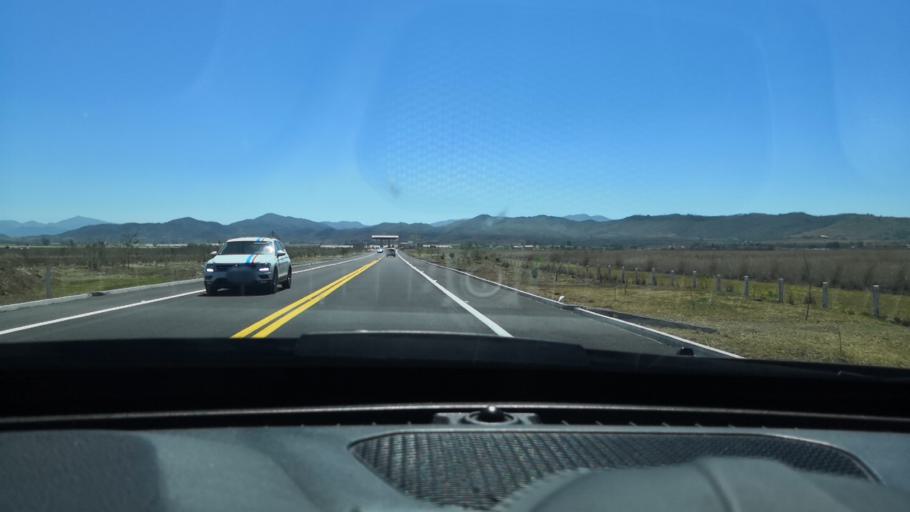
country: MX
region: Nayarit
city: Compostela
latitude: 21.2090
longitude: -104.8858
